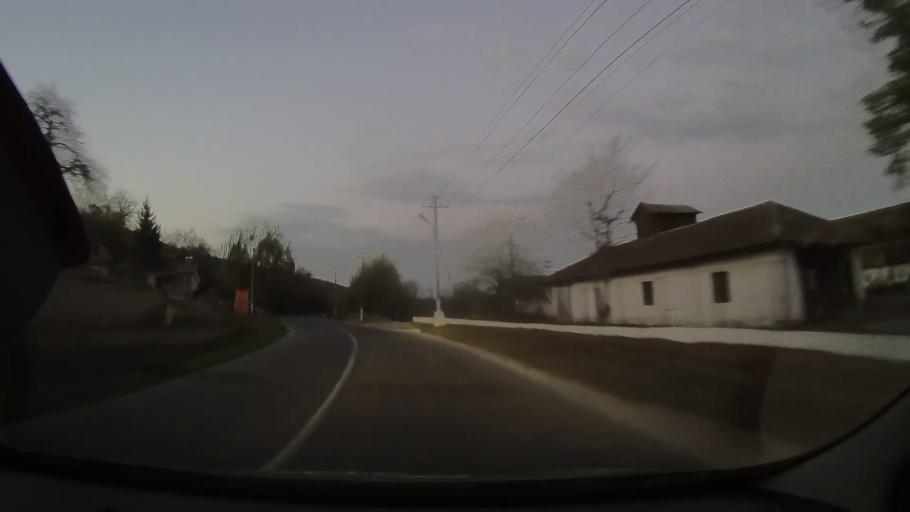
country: RO
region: Constanta
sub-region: Comuna Ion Corvin
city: Ion Corvin
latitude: 44.0988
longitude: 27.7550
